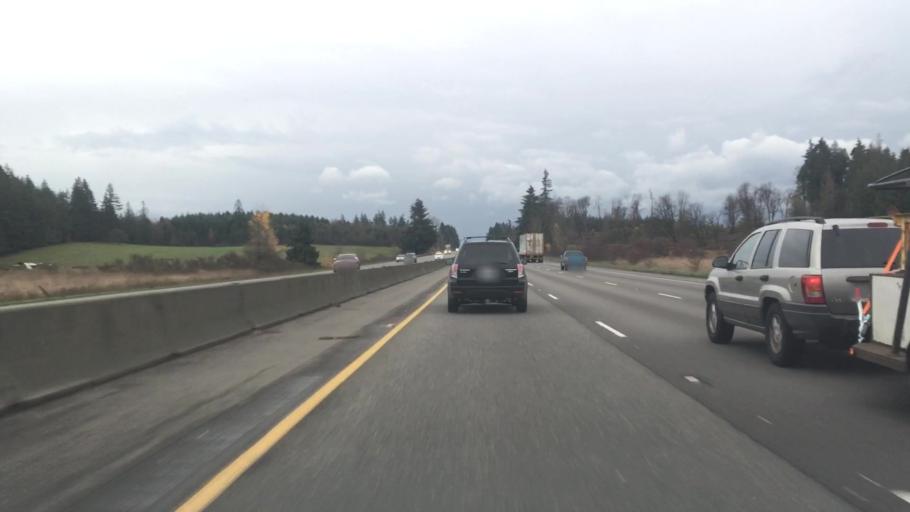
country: US
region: Washington
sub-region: Thurston County
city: Tumwater
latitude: 46.9151
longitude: -122.9506
